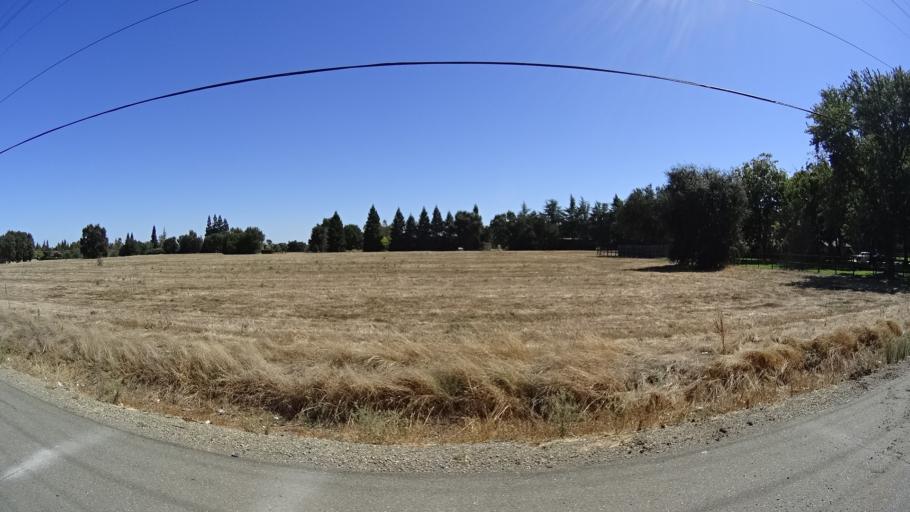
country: US
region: California
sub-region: Sacramento County
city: Wilton
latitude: 38.4293
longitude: -121.3029
